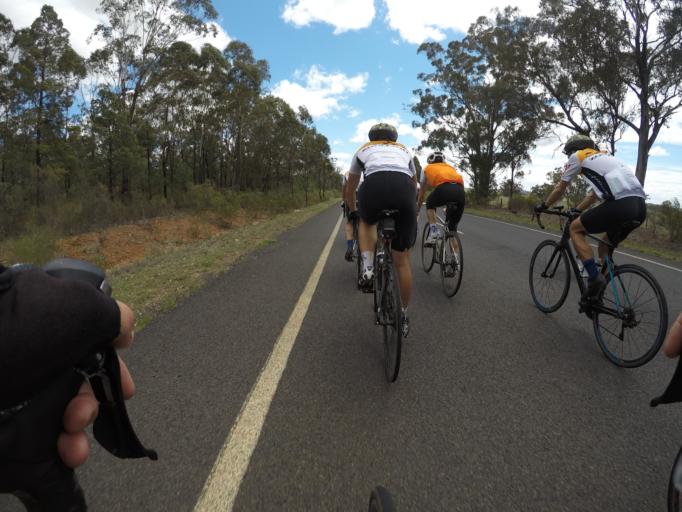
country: AU
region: New South Wales
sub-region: Dubbo Municipality
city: Dubbo
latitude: -32.4263
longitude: 148.5763
